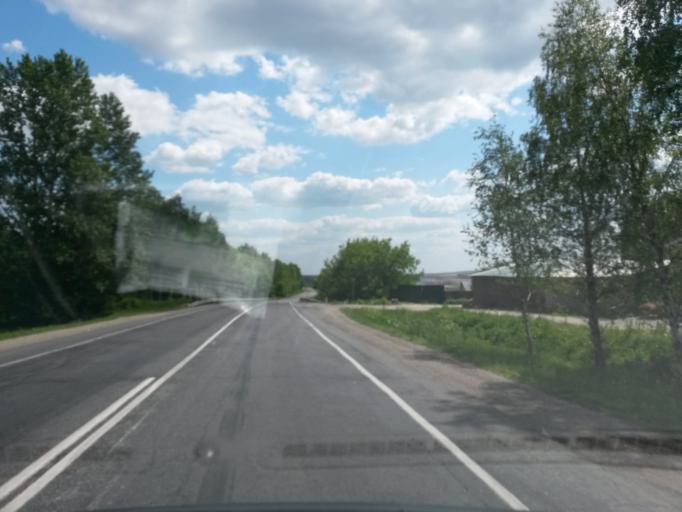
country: RU
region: Jaroslavl
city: Yaroslavl
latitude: 57.5550
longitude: 39.8747
